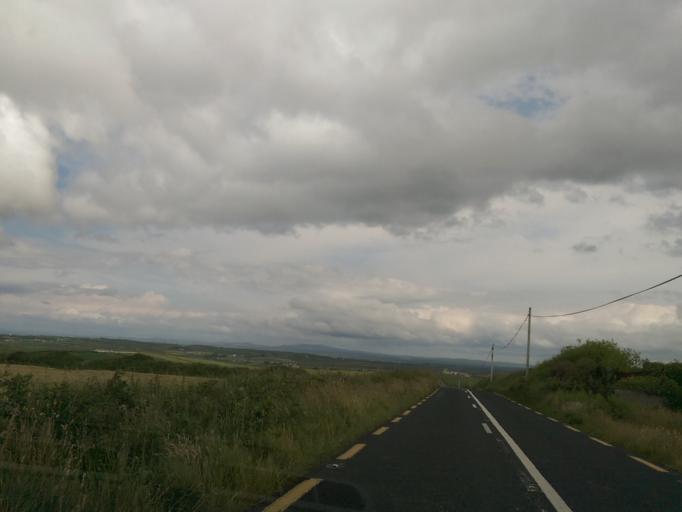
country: IE
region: Munster
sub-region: An Clar
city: Kilrush
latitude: 52.7022
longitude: -9.6196
